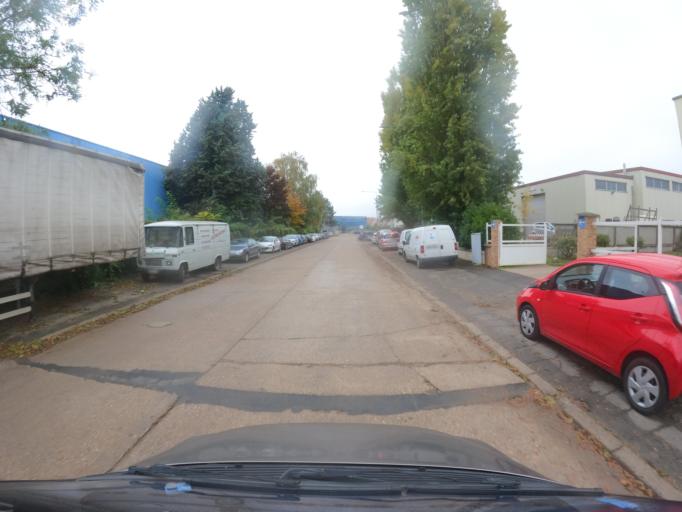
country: FR
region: Ile-de-France
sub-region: Departement du Val-de-Marne
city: Chennevieres-sur-Marne
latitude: 48.7964
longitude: 2.5407
